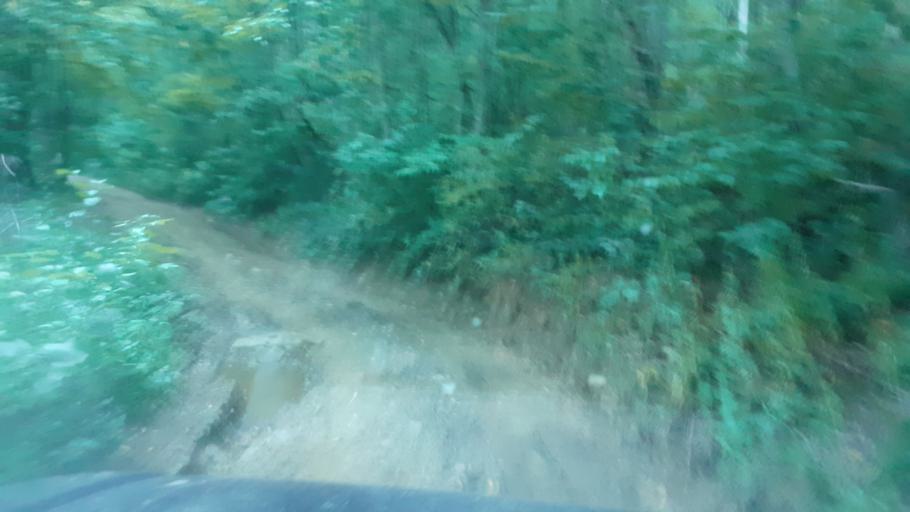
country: RU
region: Krasnodarskiy
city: Pshada
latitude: 44.6569
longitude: 38.4455
